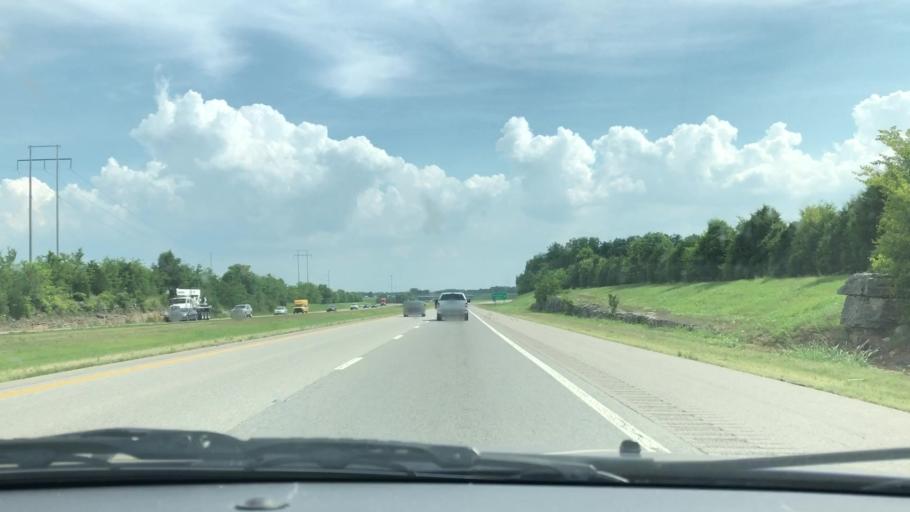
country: US
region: Tennessee
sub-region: Wilson County
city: Rural Hill
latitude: 36.0772
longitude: -86.4293
